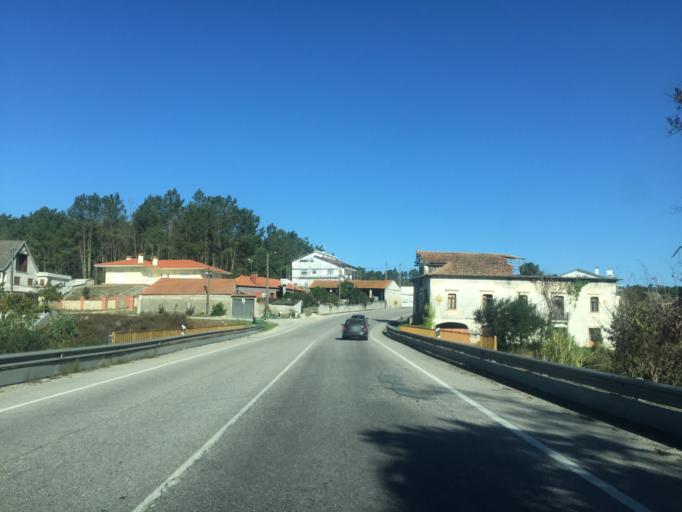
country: PT
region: Leiria
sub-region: Leiria
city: Monte Redondo
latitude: 39.9093
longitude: -8.8213
